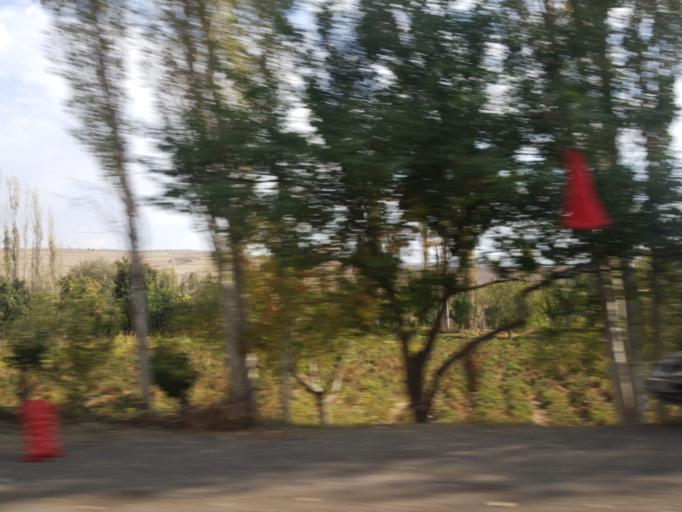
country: TR
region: Corum
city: Sungurlu
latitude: 40.2150
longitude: 34.5535
